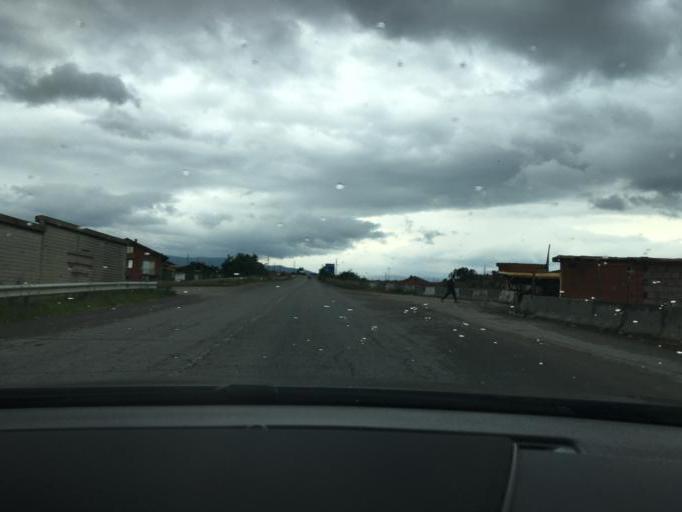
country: BG
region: Kyustendil
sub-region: Obshtina Kyustendil
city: Kyustendil
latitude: 42.2987
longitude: 22.7156
